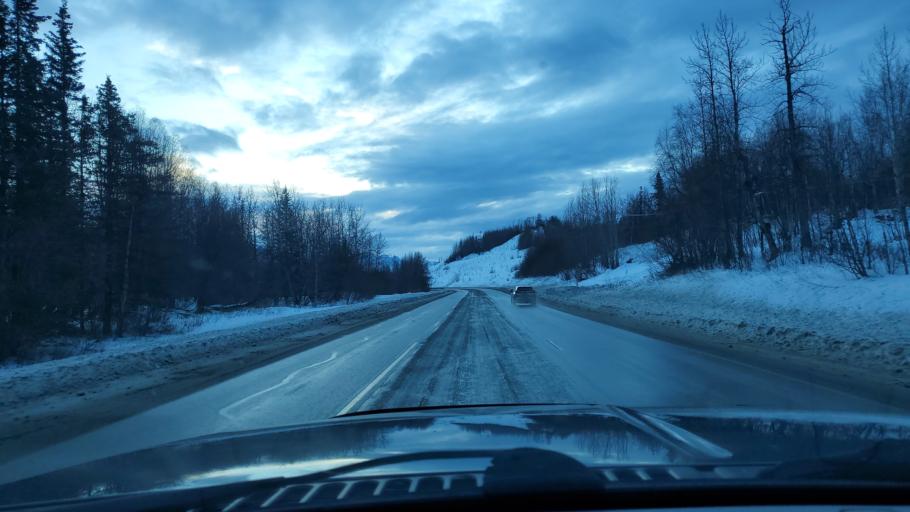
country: US
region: Alaska
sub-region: Matanuska-Susitna Borough
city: Lazy Mountain
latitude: 61.7037
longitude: -148.9501
